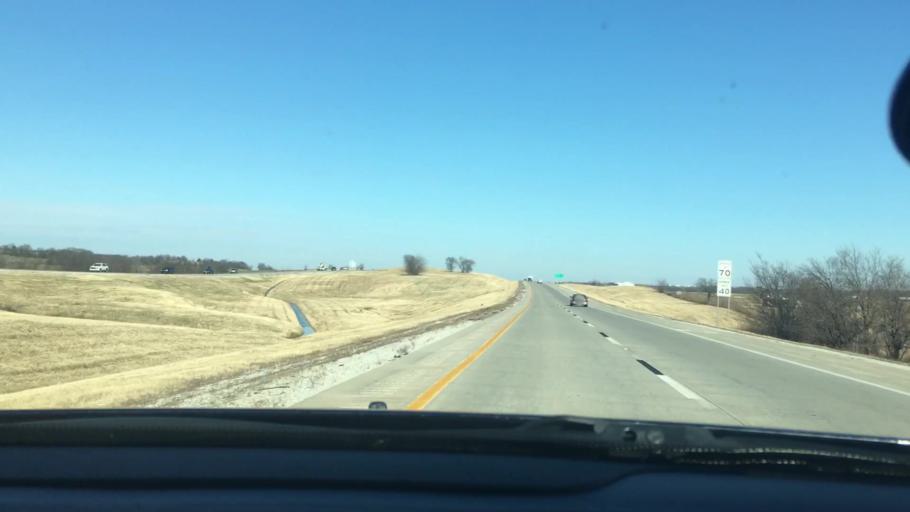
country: US
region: Oklahoma
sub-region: Carter County
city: Ardmore
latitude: 34.0798
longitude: -97.1495
